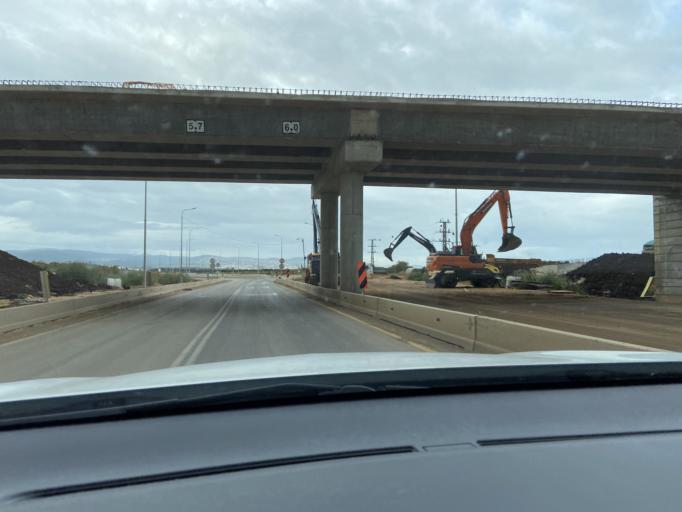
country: IL
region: Northern District
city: El Mazra`a
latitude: 32.9779
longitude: 35.1133
